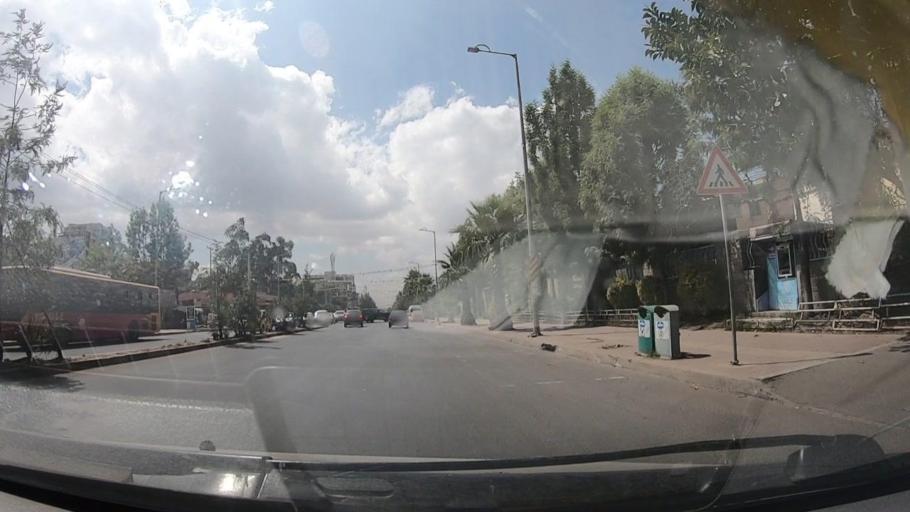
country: ET
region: Adis Abeba
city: Addis Ababa
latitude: 8.9930
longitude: 38.7269
